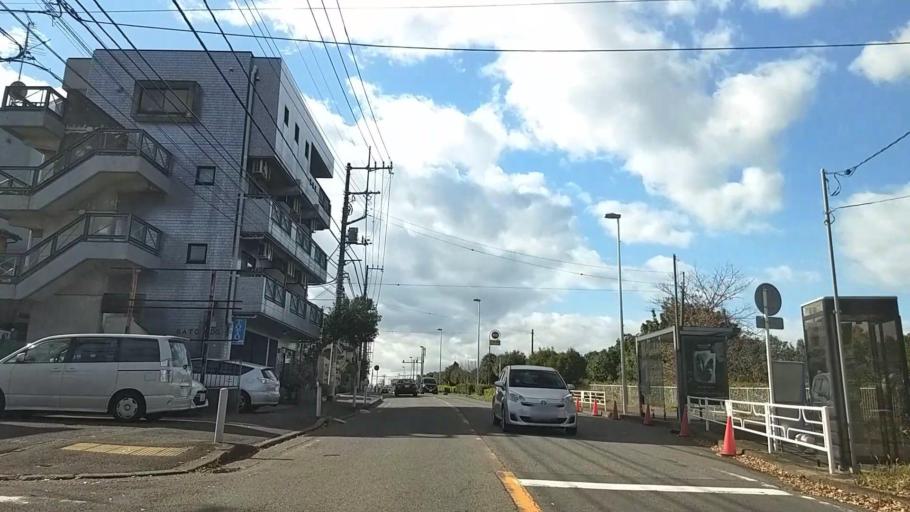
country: JP
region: Kanagawa
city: Yokohama
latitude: 35.4936
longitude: 139.6159
